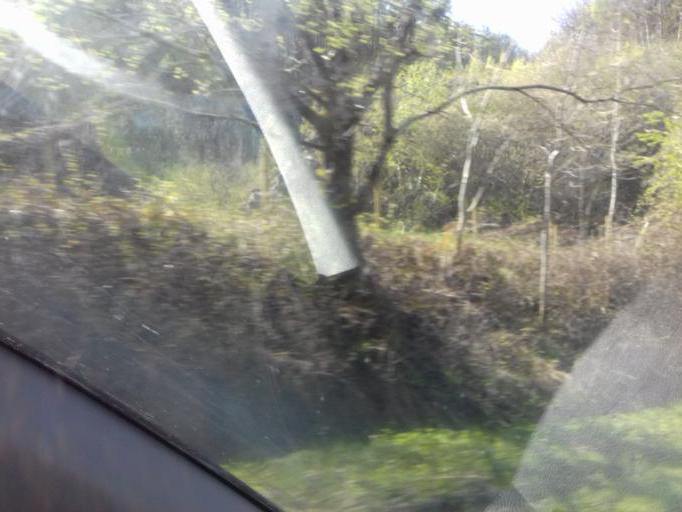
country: GB
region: Northern Ireland
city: Irvinestown
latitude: 54.4177
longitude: -7.7321
